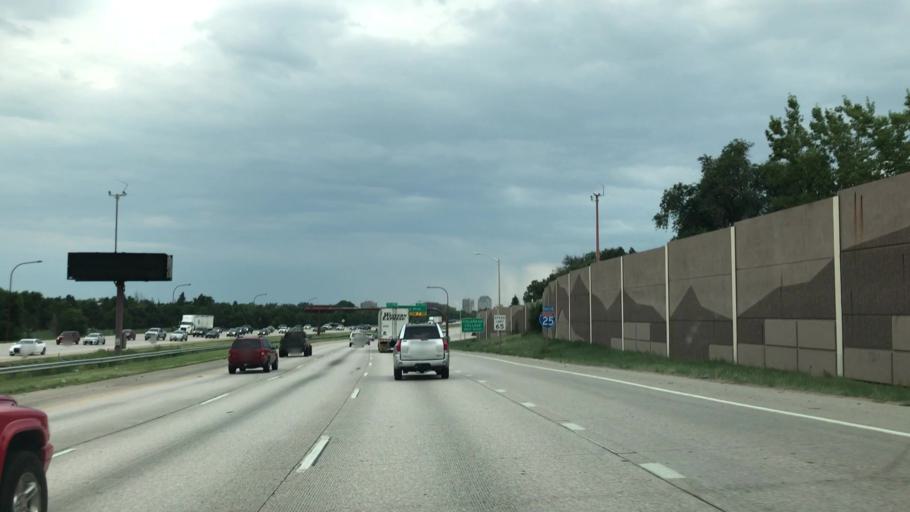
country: US
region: Colorado
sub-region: El Paso County
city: Colorado Springs
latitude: 38.8566
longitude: -104.8339
